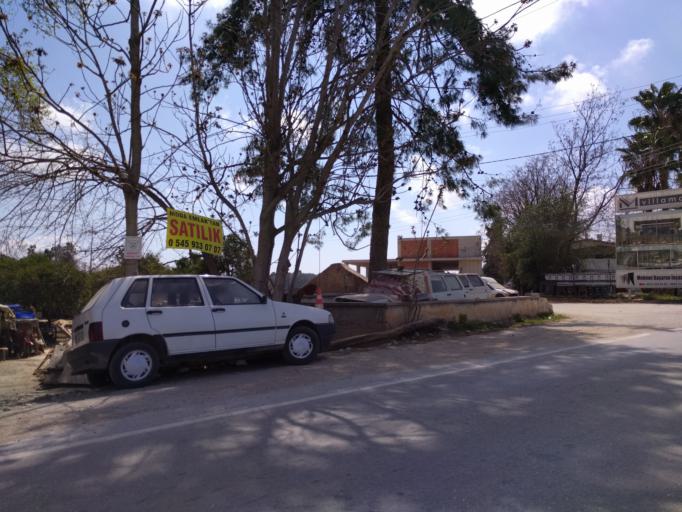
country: TR
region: Antalya
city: Cakirlar
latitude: 36.8951
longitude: 30.6060
